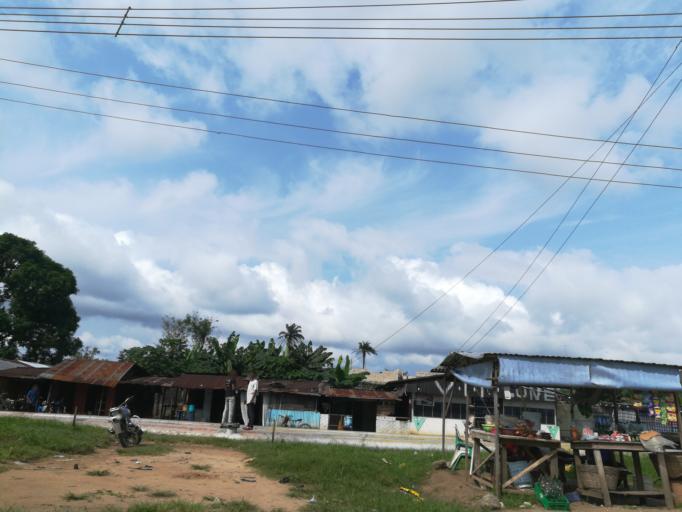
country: NG
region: Rivers
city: Okrika
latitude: 4.7545
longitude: 7.0993
